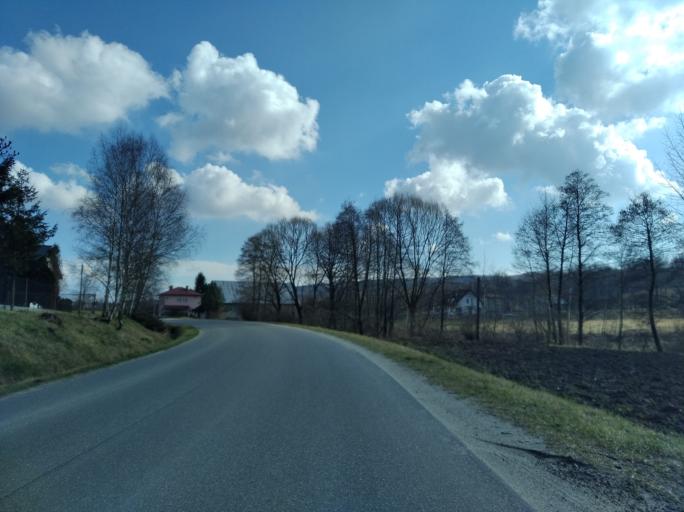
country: PL
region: Subcarpathian Voivodeship
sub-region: Powiat jasielski
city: Kolaczyce
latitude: 49.8570
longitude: 21.4872
